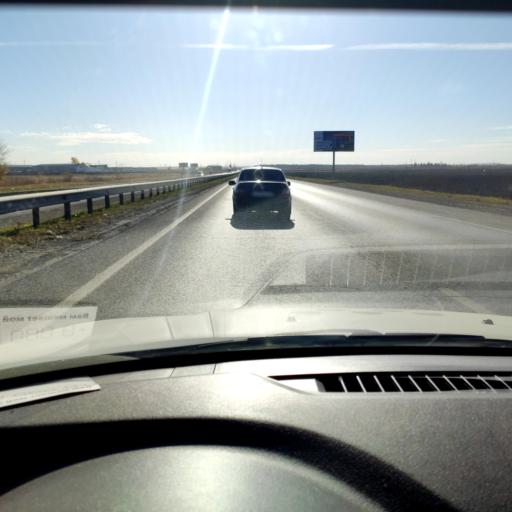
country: RU
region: Samara
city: Tol'yatti
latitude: 53.5626
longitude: 49.4973
